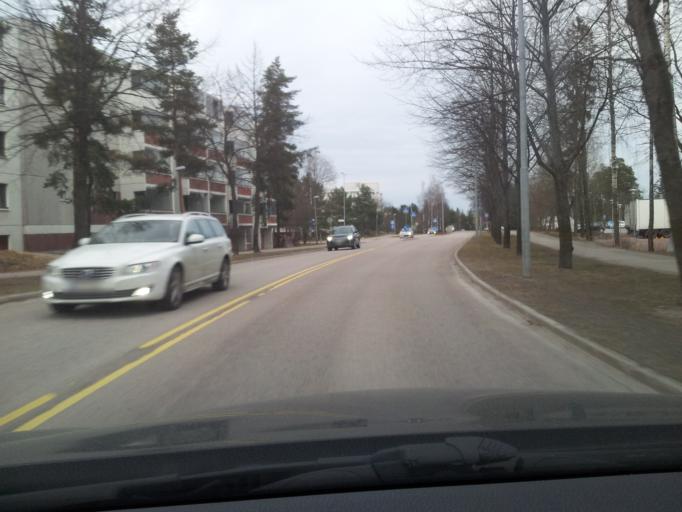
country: FI
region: Uusimaa
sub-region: Helsinki
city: Espoo
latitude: 60.1462
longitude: 24.6550
